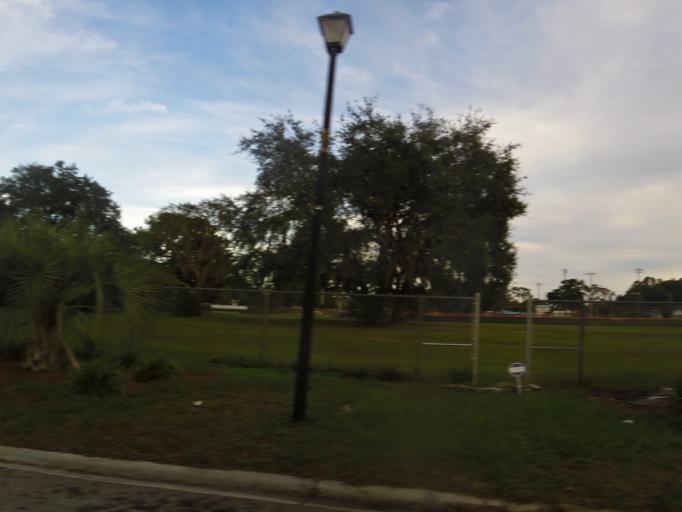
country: US
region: Florida
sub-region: Saint Johns County
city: Fruit Cove
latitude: 30.1572
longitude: -81.5457
